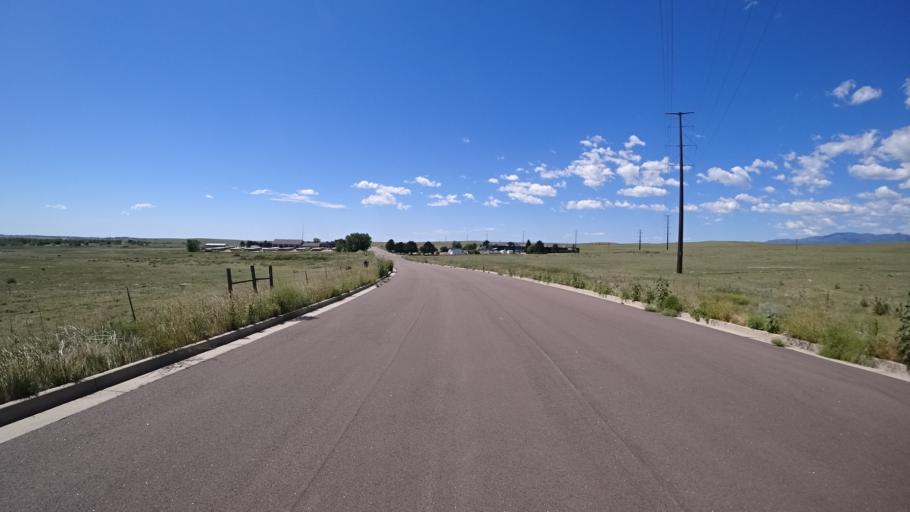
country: US
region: Colorado
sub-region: El Paso County
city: Security-Widefield
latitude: 38.7698
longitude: -104.6692
